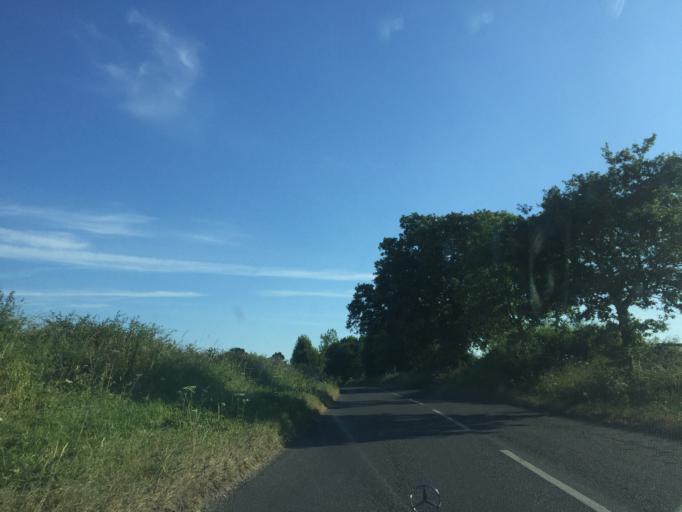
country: GB
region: England
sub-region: Oxfordshire
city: Watlington
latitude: 51.6099
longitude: -0.9923
